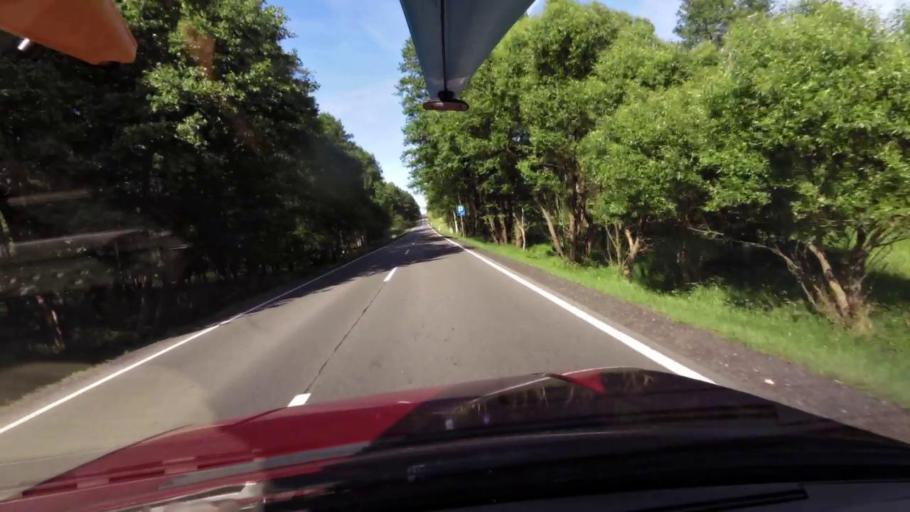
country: PL
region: Pomeranian Voivodeship
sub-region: Powiat bytowski
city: Trzebielino
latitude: 54.1450
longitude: 17.0326
